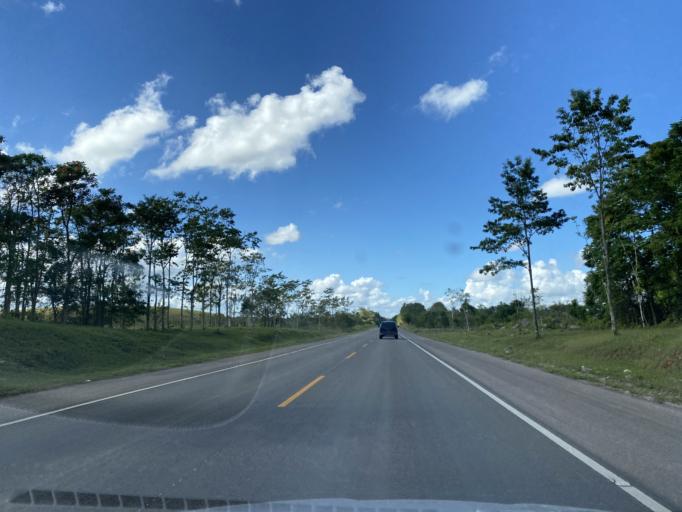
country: DO
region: Monte Plata
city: Sabana Grande de Boya
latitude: 18.9711
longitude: -69.7814
